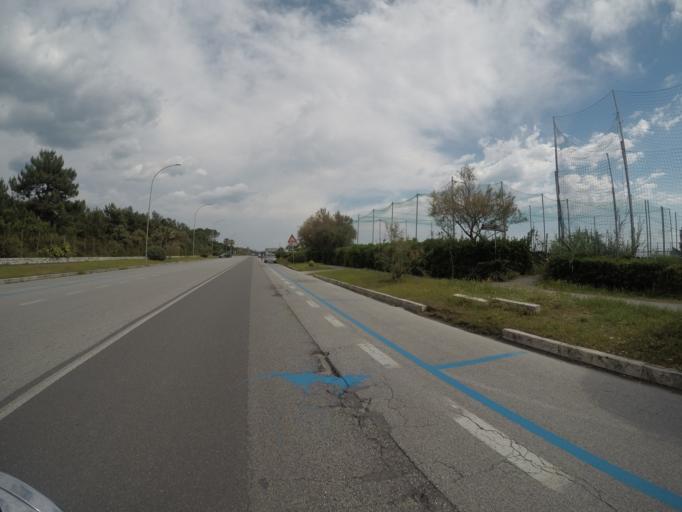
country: IT
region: Tuscany
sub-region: Provincia di Massa-Carrara
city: Massa
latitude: 43.9991
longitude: 10.1131
